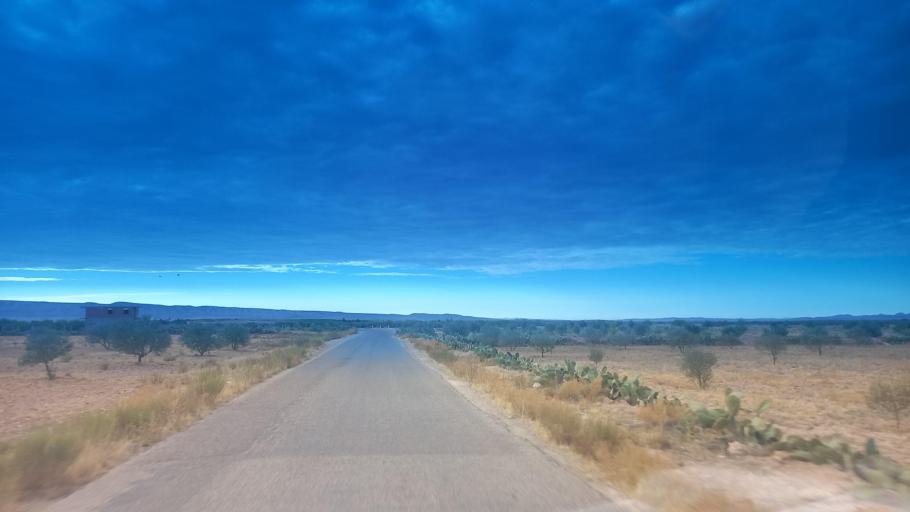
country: TN
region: Al Qasrayn
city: Sbiba
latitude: 35.3874
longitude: 9.0297
